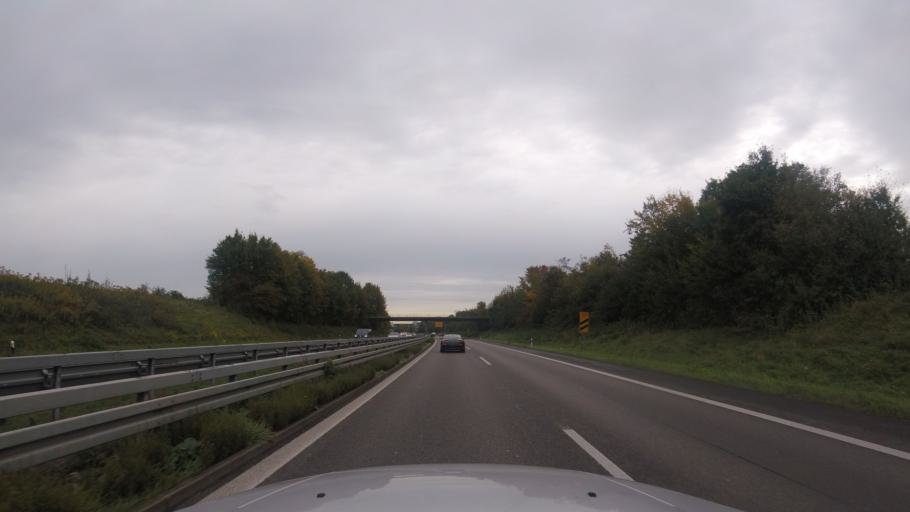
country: DE
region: Baden-Wuerttemberg
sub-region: Regierungsbezirk Stuttgart
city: Weinstadt-Endersbach
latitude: 48.8142
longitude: 9.3431
